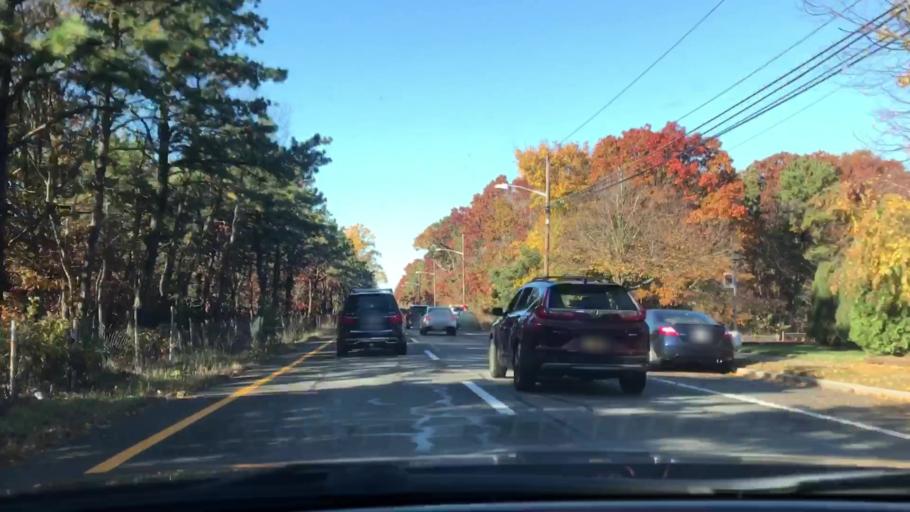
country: US
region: New York
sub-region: Suffolk County
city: Islandia
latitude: 40.8107
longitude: -73.1509
